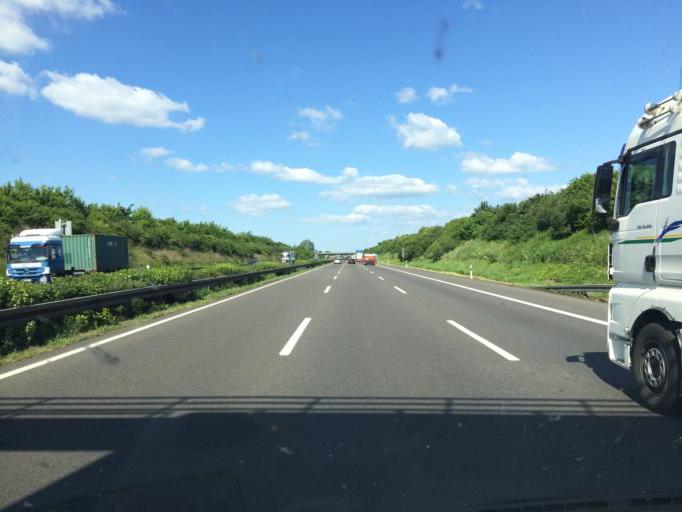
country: DE
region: Lower Saxony
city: Gross Munzel
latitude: 52.3837
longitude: 9.4700
